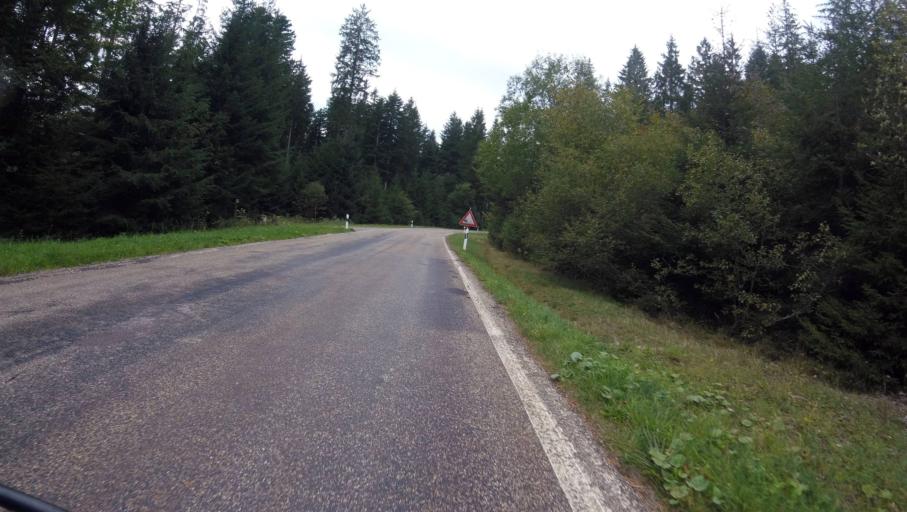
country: DE
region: Baden-Wuerttemberg
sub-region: Karlsruhe Region
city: Simmersfeld
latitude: 48.6068
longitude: 8.4713
